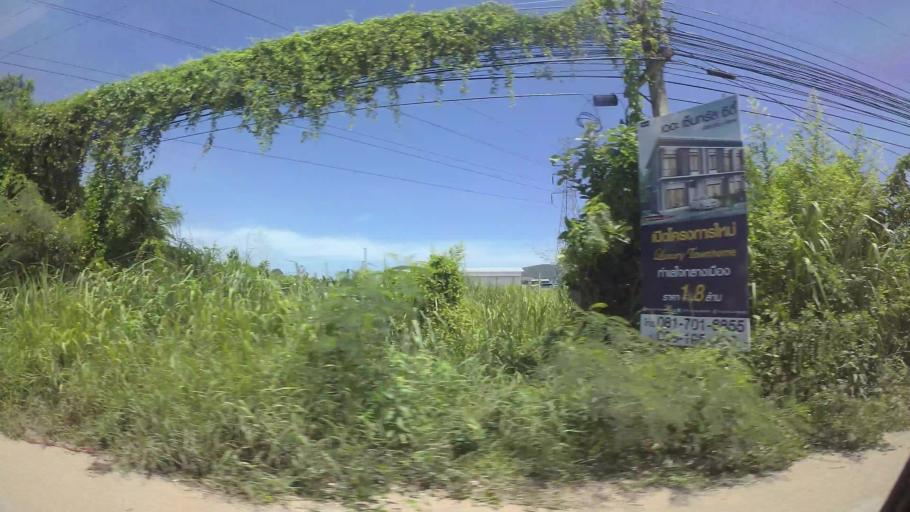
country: TH
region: Chon Buri
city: Si Racha
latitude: 13.1281
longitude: 100.9537
